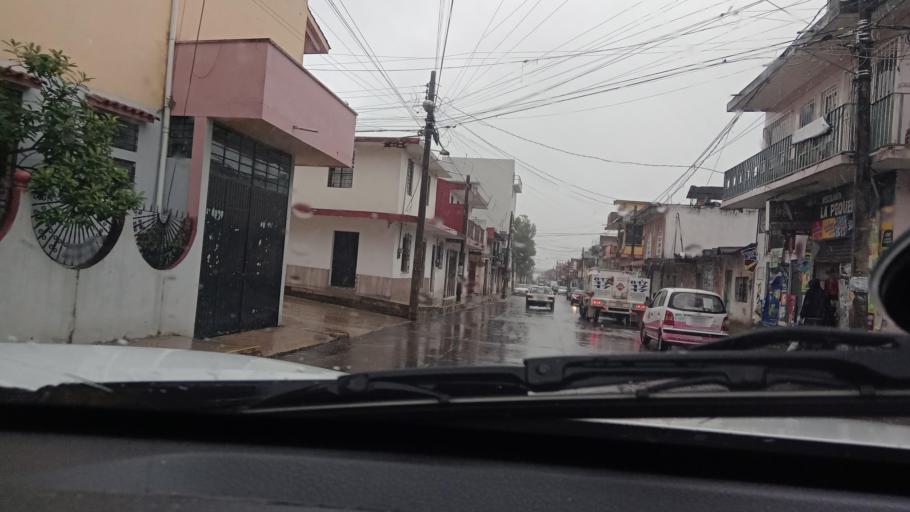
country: MX
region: Veracruz
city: Coatepec
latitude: 19.4557
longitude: -96.9689
